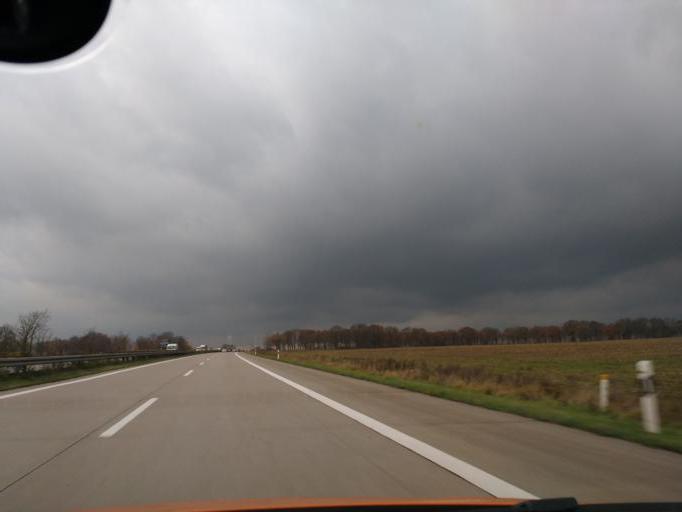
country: DE
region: Brandenburg
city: Heiligengrabe
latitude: 53.1722
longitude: 12.3307
